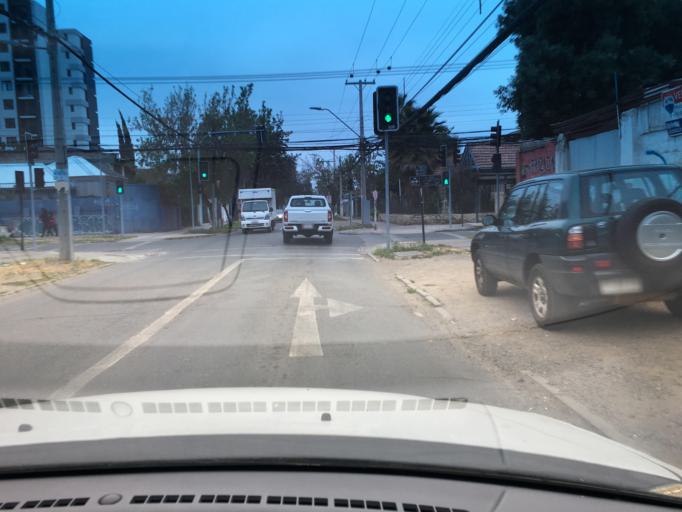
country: CL
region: Santiago Metropolitan
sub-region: Provincia de Santiago
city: Villa Presidente Frei, Nunoa, Santiago, Chile
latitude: -33.4791
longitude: -70.6015
